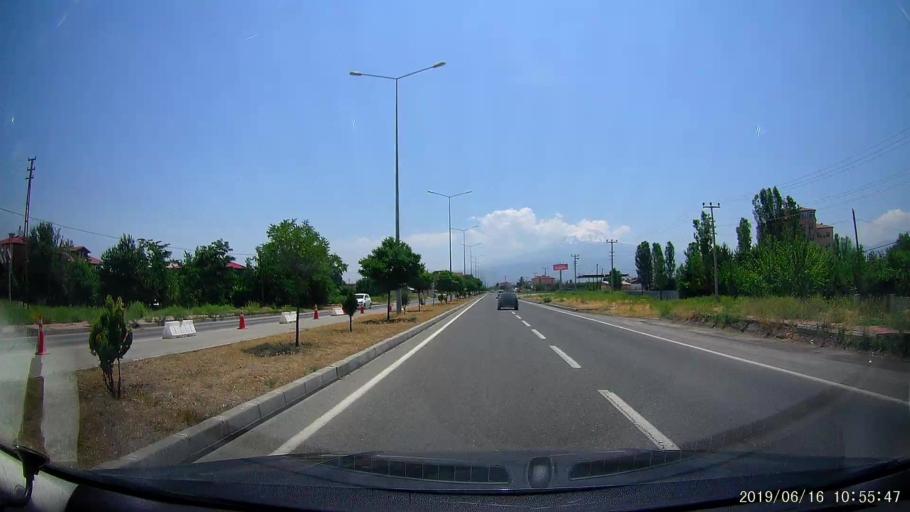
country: TR
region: Igdir
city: Igdir
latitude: 39.9344
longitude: 44.0141
